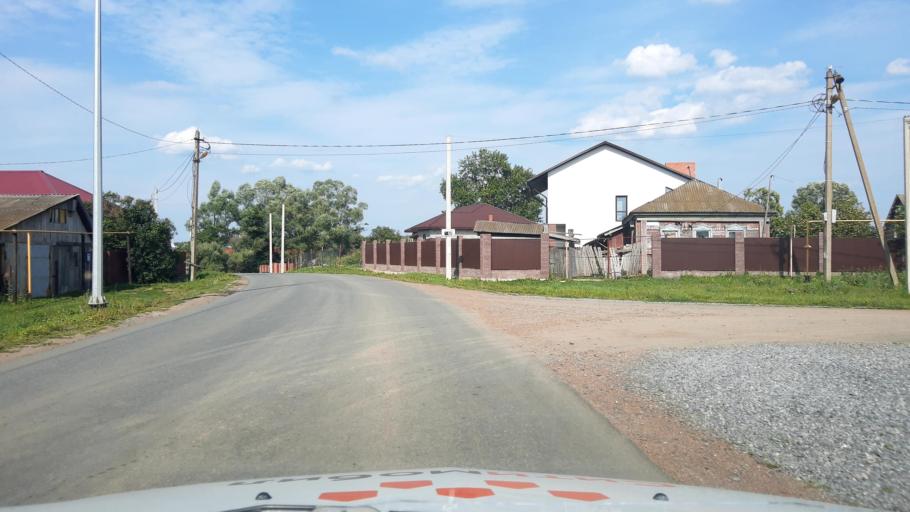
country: RU
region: Bashkortostan
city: Kabakovo
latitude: 54.6583
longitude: 56.1987
